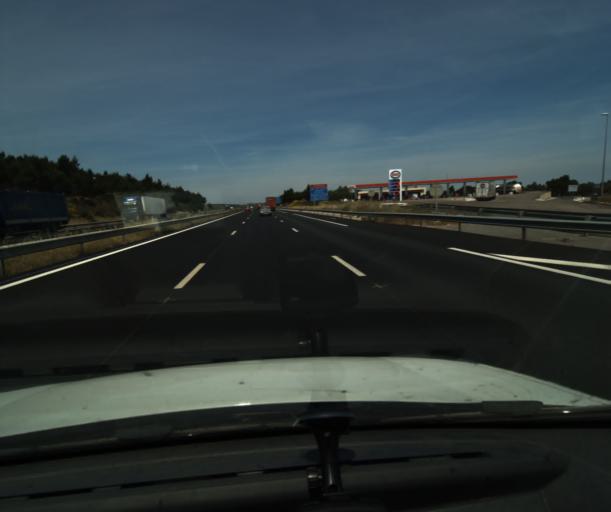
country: FR
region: Languedoc-Roussillon
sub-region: Departement de l'Aude
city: Leucate
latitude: 42.9490
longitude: 2.9709
